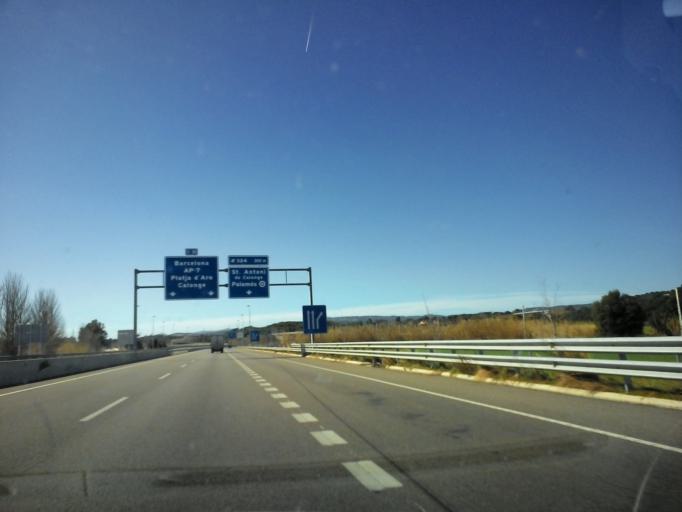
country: ES
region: Catalonia
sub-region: Provincia de Girona
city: Palamos
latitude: 41.8605
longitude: 3.1263
